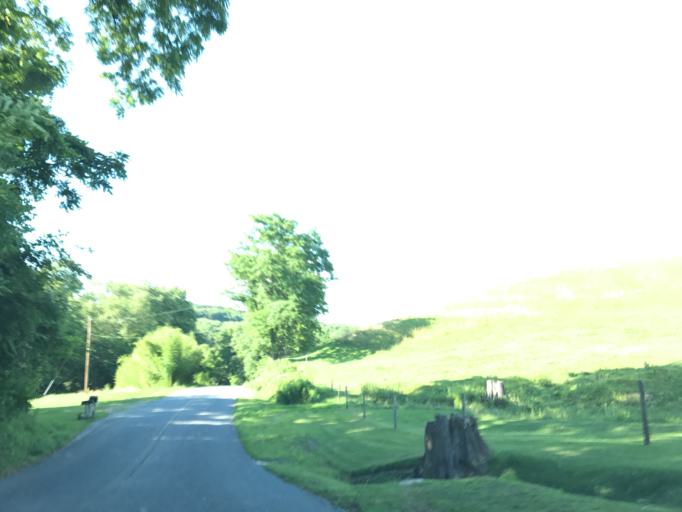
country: US
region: Pennsylvania
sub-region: Lancaster County
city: Conestoga
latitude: 39.9211
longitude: -76.3377
